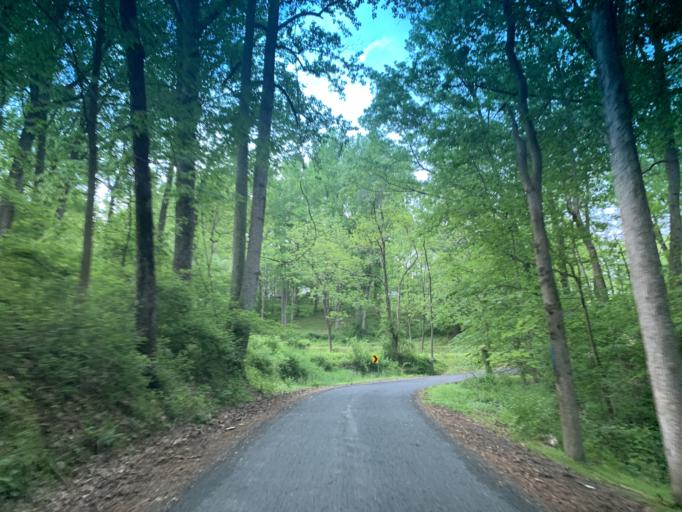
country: US
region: Pennsylvania
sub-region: York County
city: Susquehanna Trails
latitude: 39.7042
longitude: -76.2612
